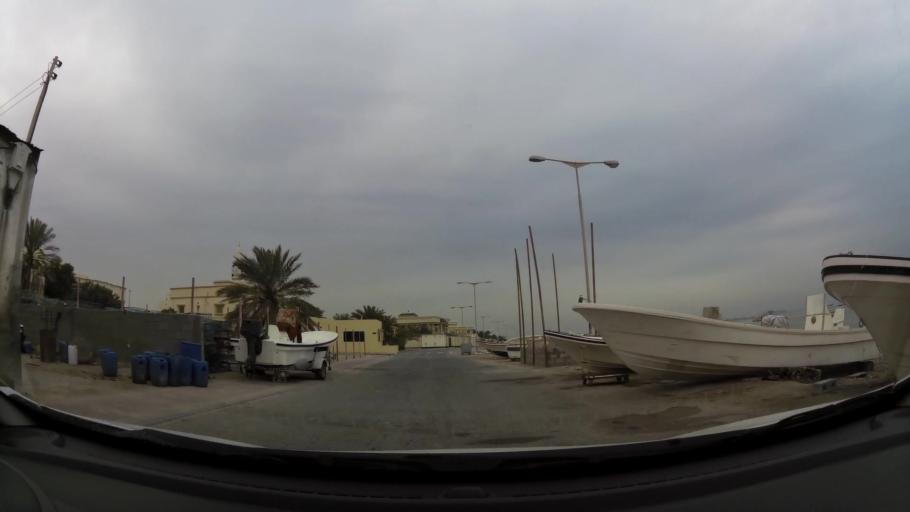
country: BH
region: Northern
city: Ar Rifa'
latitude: 26.0574
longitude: 50.6190
